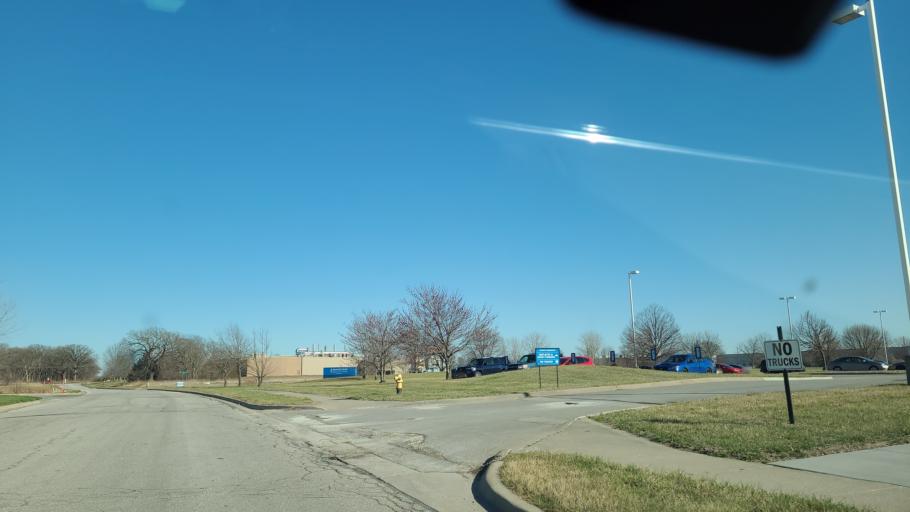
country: US
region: Kansas
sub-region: Douglas County
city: Lawrence
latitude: 38.9474
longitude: -95.1823
